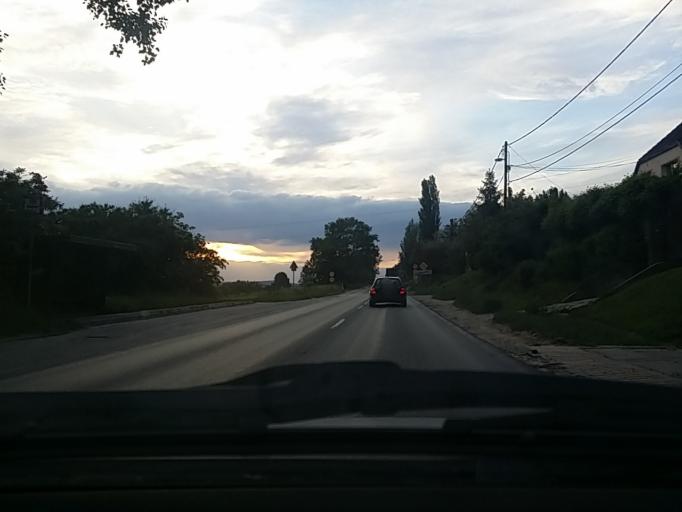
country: HU
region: Pest
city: Pilisborosjeno
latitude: 47.5918
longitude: 18.9848
